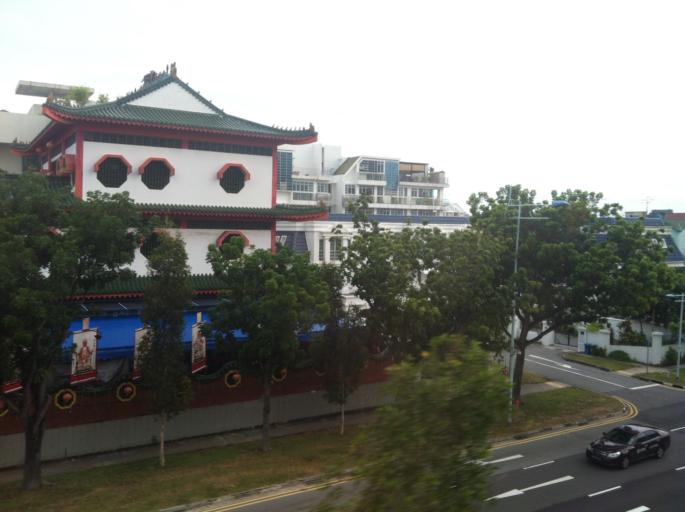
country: SG
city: Singapore
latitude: 1.3204
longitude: 103.9106
